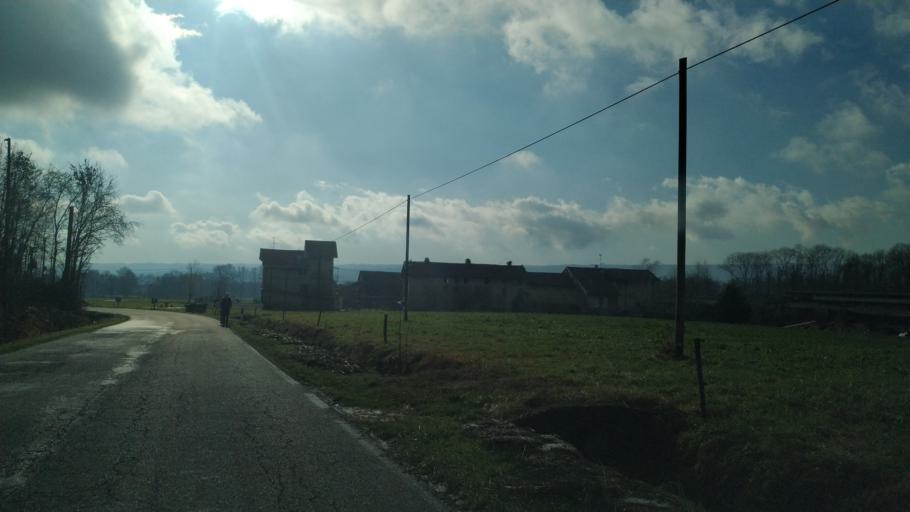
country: IT
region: Piedmont
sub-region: Provincia di Biella
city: Occhieppo Inferiore
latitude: 45.5374
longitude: 8.0252
